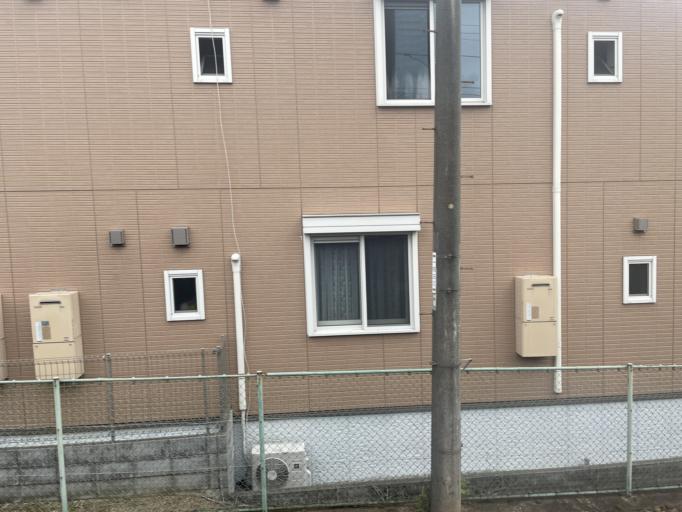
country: JP
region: Osaka
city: Ikeda
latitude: 34.8640
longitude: 135.4159
